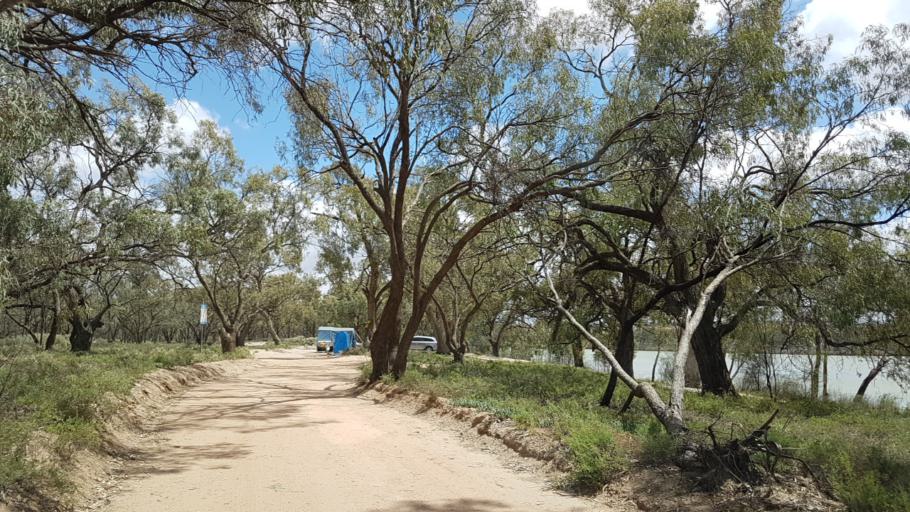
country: AU
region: South Australia
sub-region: Loxton Waikerie
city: Waikerie
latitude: -34.1627
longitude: 140.0335
